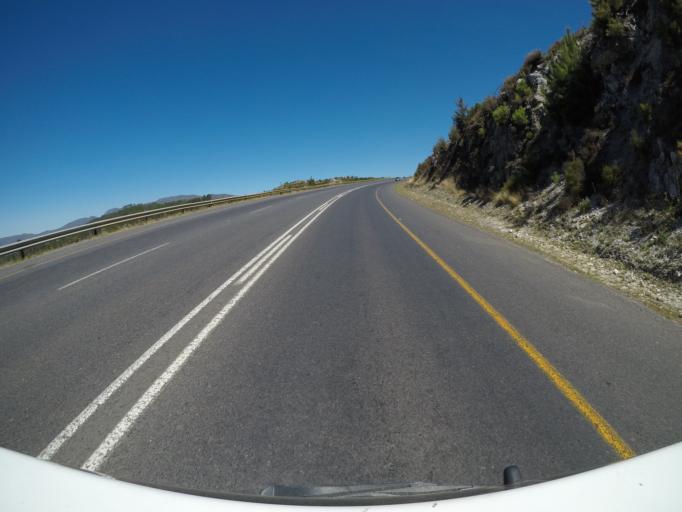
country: ZA
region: Western Cape
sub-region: Overberg District Municipality
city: Grabouw
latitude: -34.1641
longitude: 19.0059
